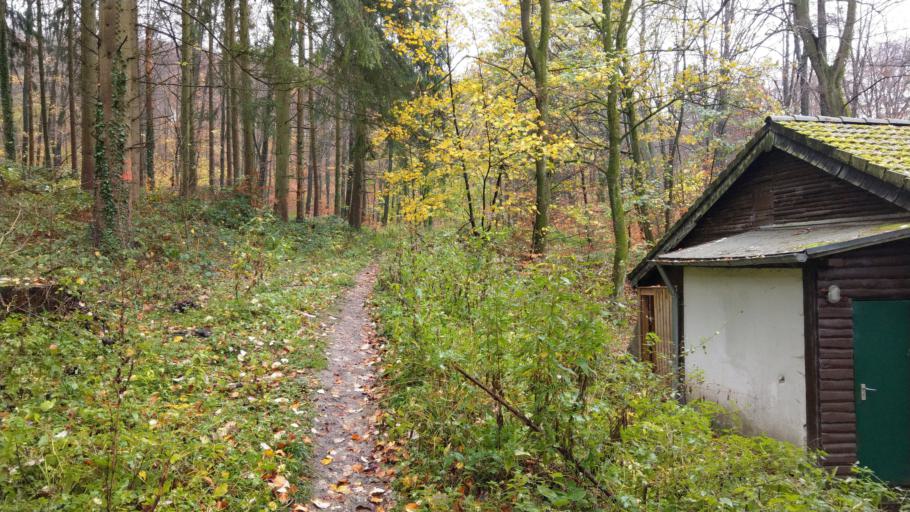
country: DE
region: North Rhine-Westphalia
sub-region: Regierungsbezirk Koln
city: Aachen
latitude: 50.7428
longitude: 6.0665
